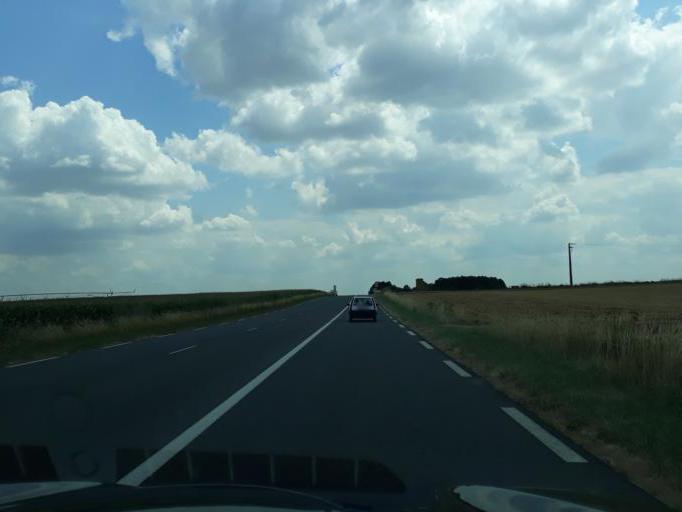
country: FR
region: Centre
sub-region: Departement du Cher
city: Saint-Germain-du-Puy
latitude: 47.0747
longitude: 2.4837
